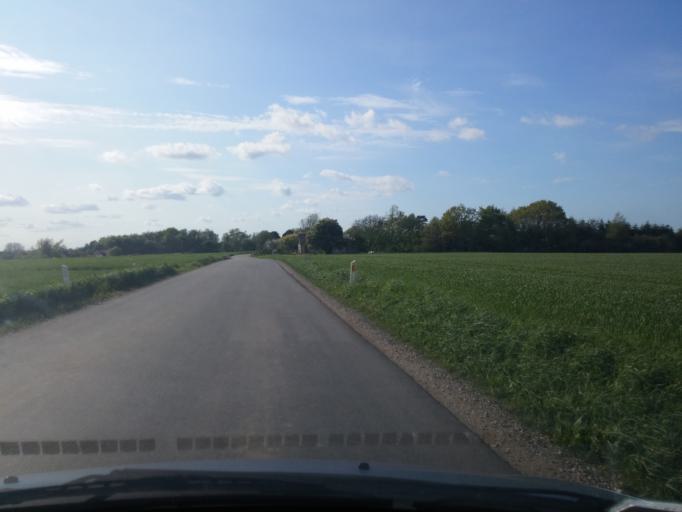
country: DK
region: South Denmark
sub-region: Kerteminde Kommune
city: Langeskov
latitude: 55.4041
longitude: 10.5920
